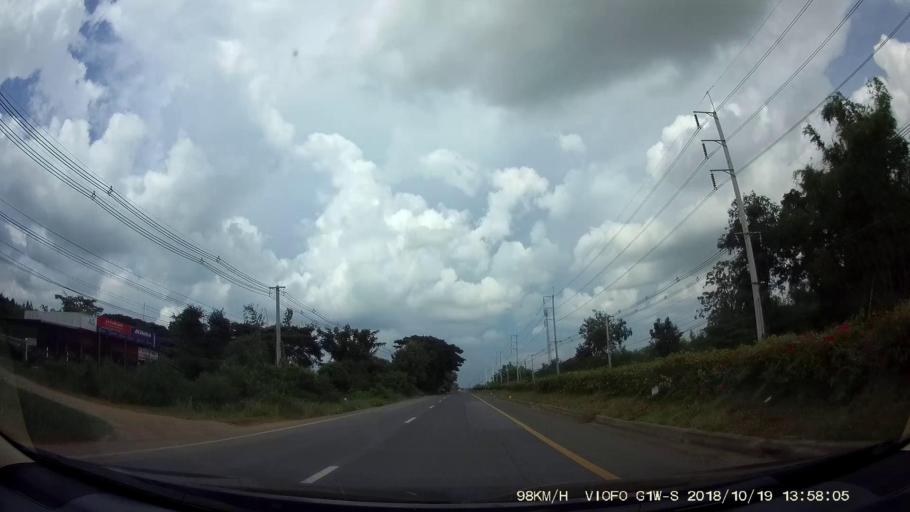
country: TH
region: Chaiyaphum
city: Chaiyaphum
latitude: 15.7948
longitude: 102.0499
